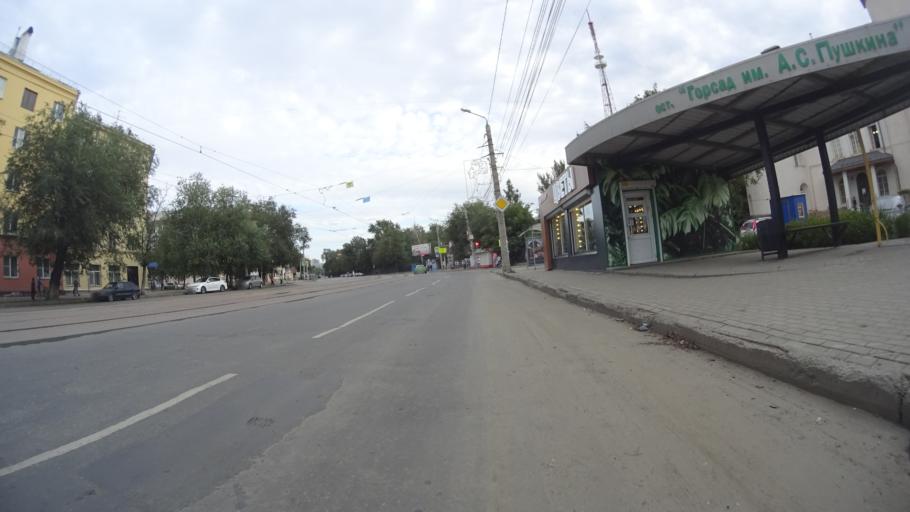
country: RU
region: Chelyabinsk
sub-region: Gorod Chelyabinsk
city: Chelyabinsk
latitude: 55.1556
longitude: 61.4068
